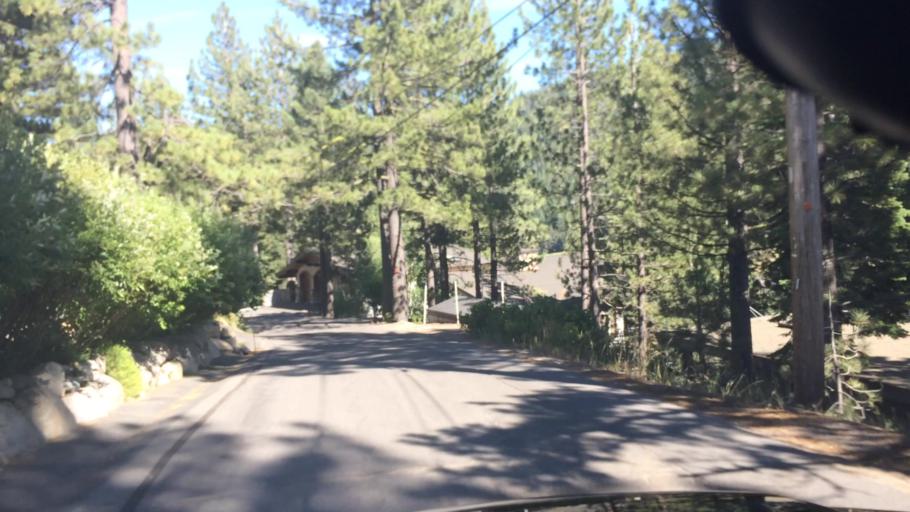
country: US
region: California
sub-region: Placer County
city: Sunnyside-Tahoe City
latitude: 39.1996
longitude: -120.2335
